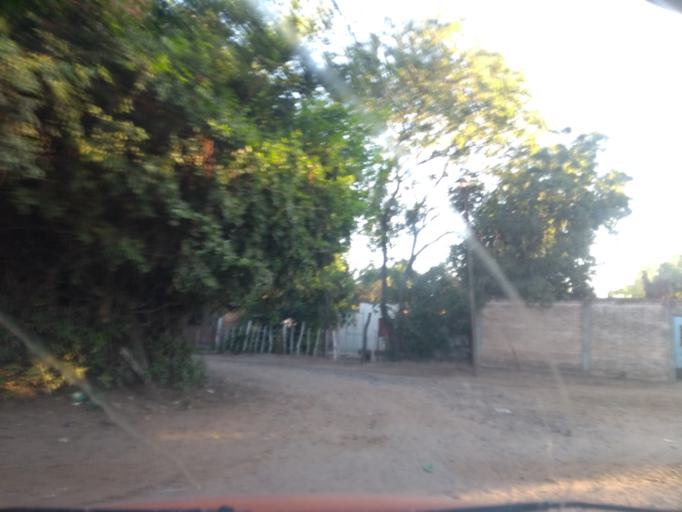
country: AR
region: Chaco
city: Resistencia
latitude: -27.4505
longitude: -58.9675
